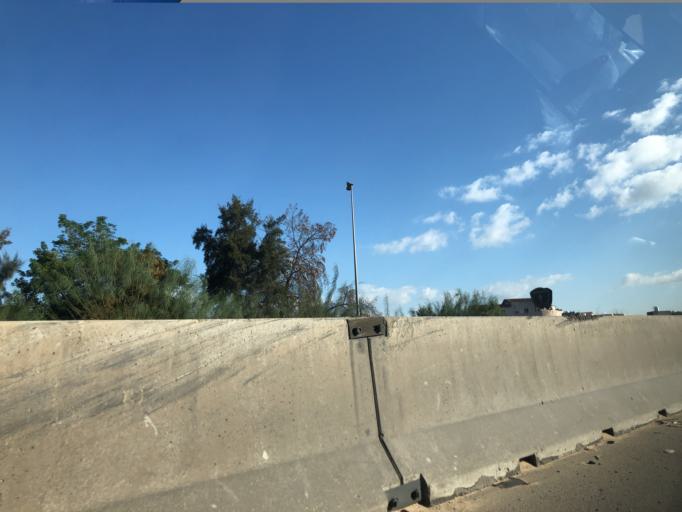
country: LY
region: Tripoli
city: Tripoli
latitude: 32.8562
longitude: 13.1978
